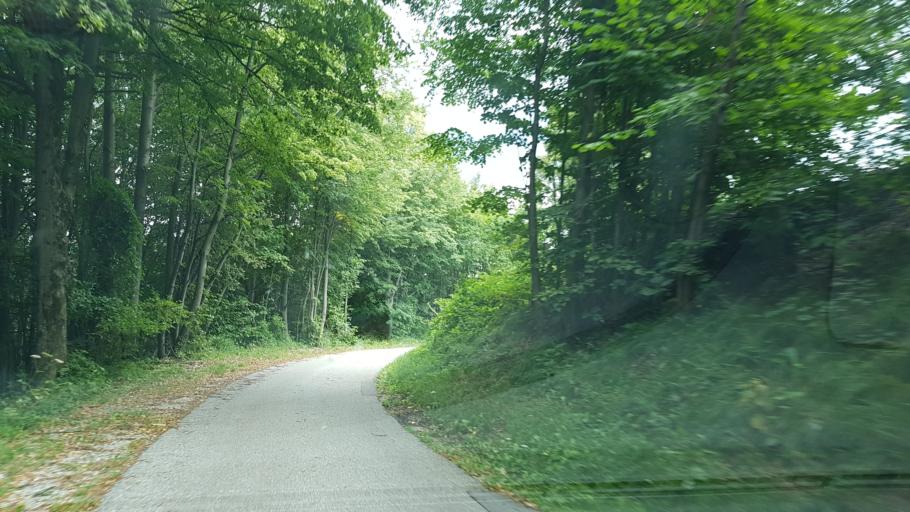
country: SI
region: Kanal
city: Deskle
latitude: 46.0669
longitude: 13.5717
